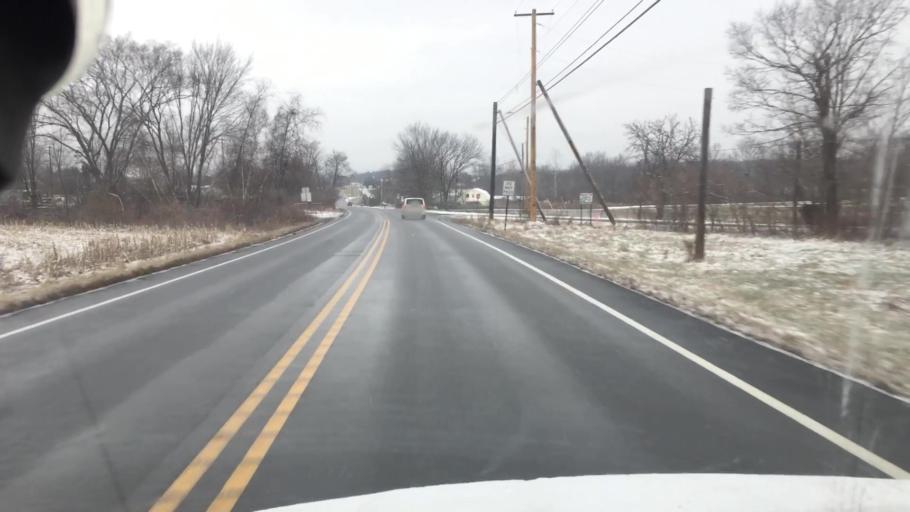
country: US
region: Pennsylvania
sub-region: Luzerne County
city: Nescopeck
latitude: 41.0428
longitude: -76.1425
